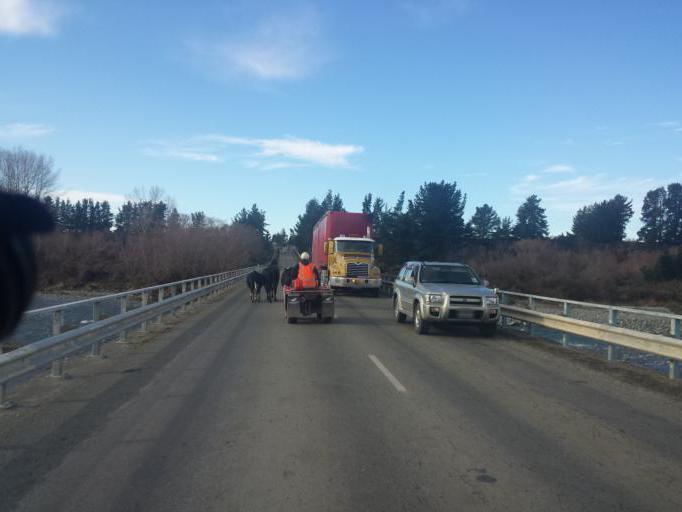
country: NZ
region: Canterbury
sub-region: Timaru District
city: Pleasant Point
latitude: -43.9737
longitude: 171.3024
